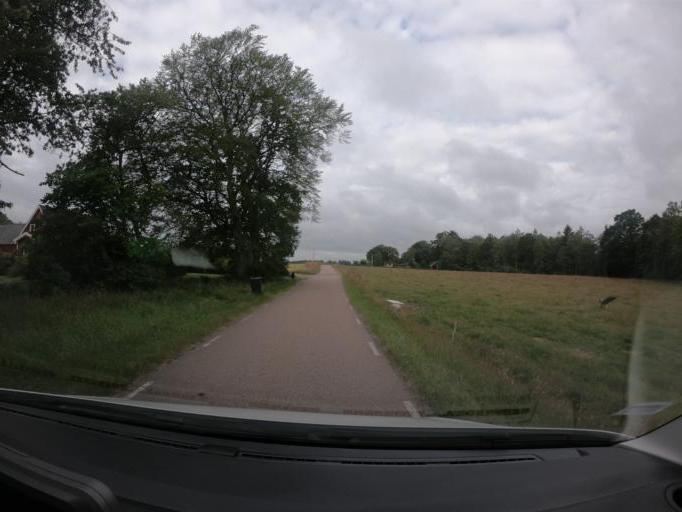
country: SE
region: Skane
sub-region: Angelholms Kommun
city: Munka-Ljungby
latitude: 56.3436
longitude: 13.0060
